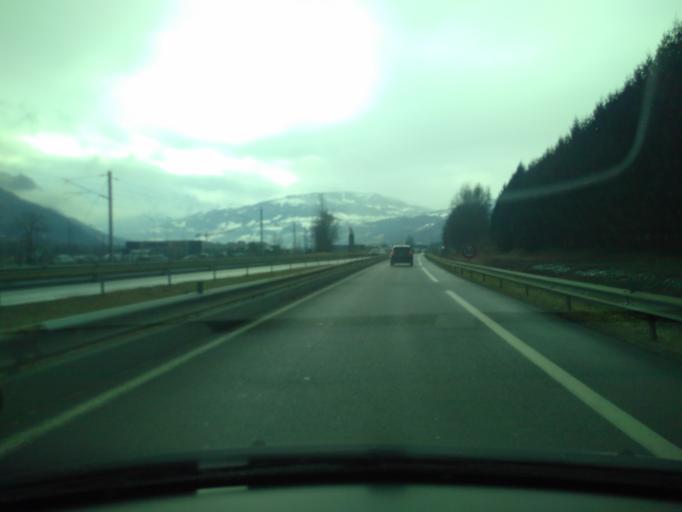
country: FR
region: Rhone-Alpes
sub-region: Departement de la Haute-Savoie
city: Sallanches
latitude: 45.9624
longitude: 6.6293
